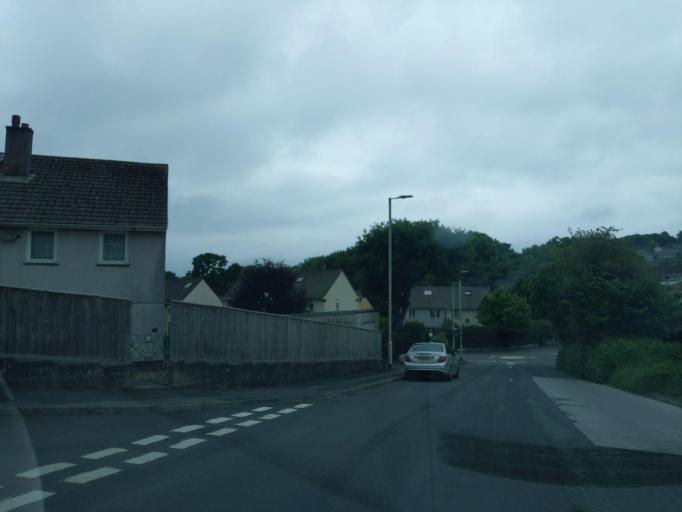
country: GB
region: England
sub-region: Devon
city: Plympton
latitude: 50.3794
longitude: -4.0391
